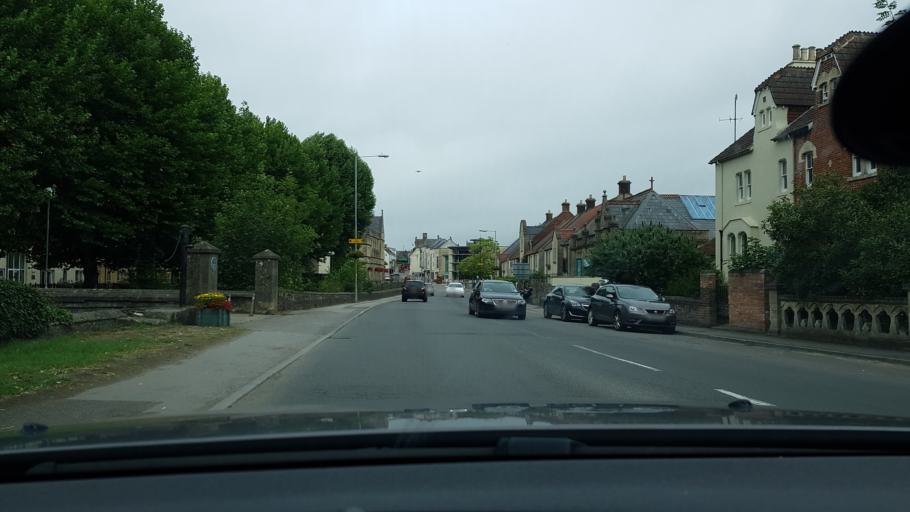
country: GB
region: England
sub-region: Wiltshire
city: Calne
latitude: 51.4364
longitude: -2.0047
